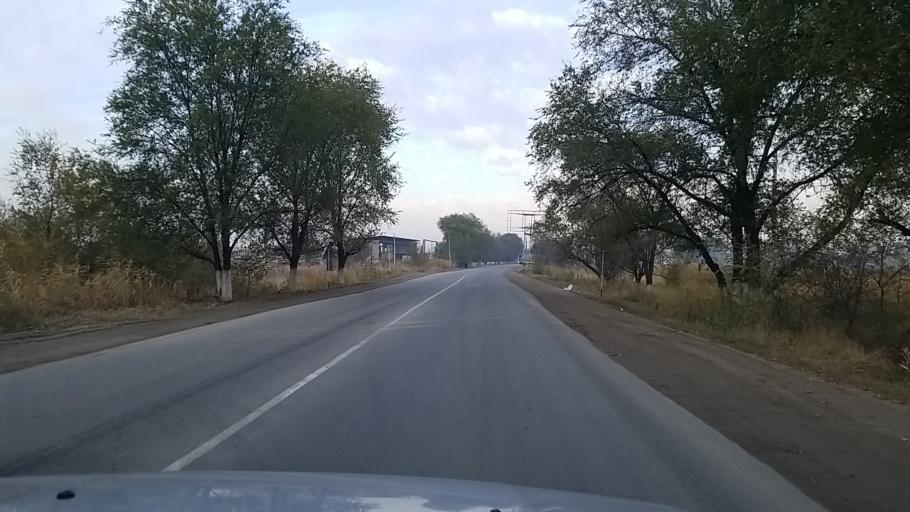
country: KZ
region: Almaty Oblysy
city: Burunday
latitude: 43.3560
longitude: 76.7967
